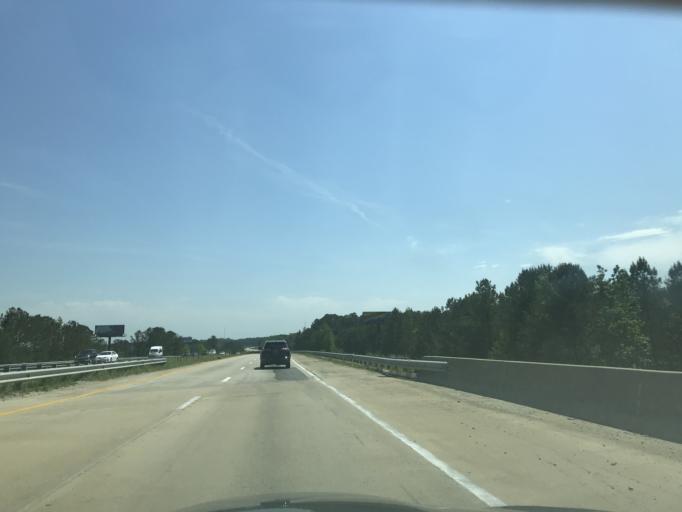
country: US
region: North Carolina
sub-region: Johnston County
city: Benson
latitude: 35.4051
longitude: -78.5238
